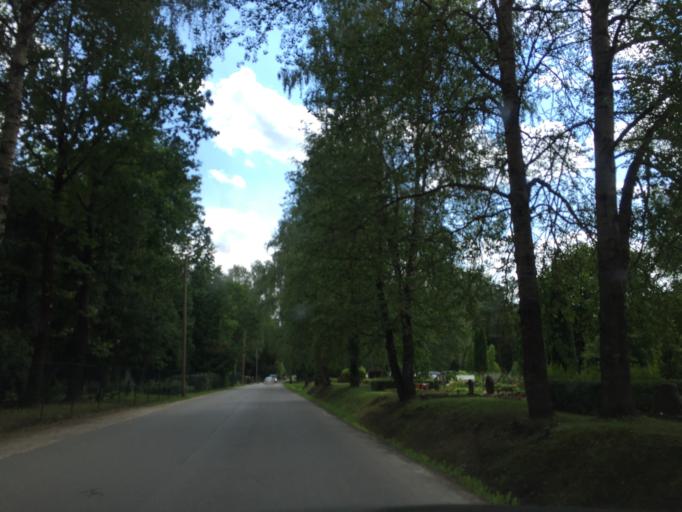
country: LV
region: Jelgava
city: Jelgava
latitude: 56.6271
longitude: 23.6853
